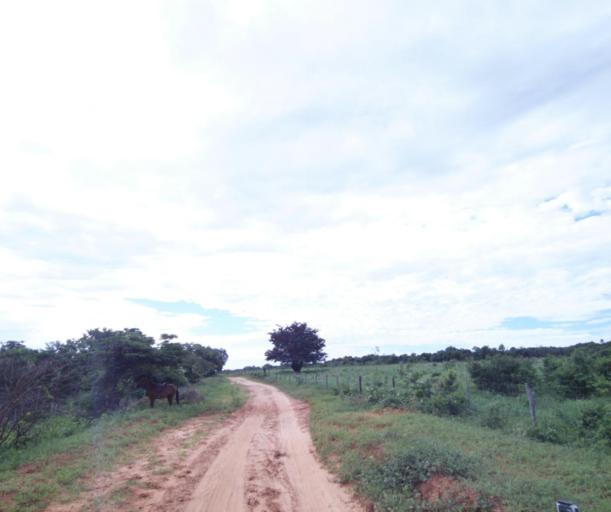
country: BR
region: Bahia
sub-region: Carinhanha
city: Carinhanha
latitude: -14.2097
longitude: -44.4558
